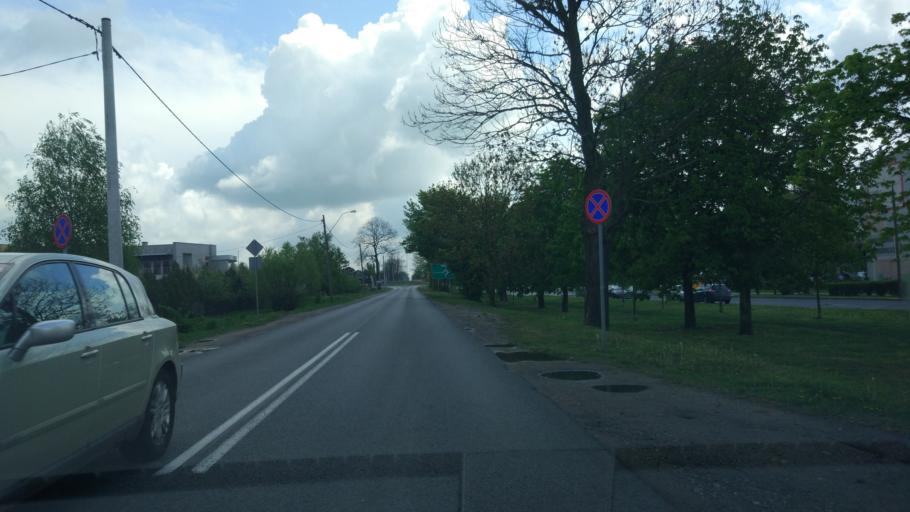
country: PL
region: Lodz Voivodeship
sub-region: Powiat kutnowski
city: Kutno
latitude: 52.2277
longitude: 19.3829
